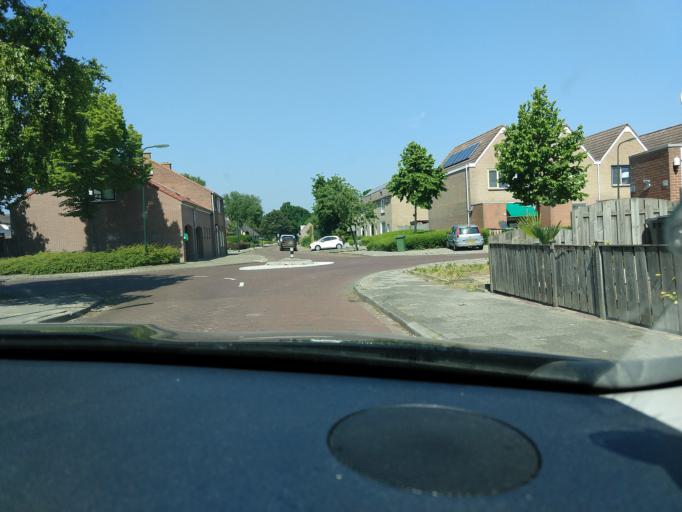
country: NL
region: Zeeland
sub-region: Gemeente Reimerswaal
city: Yerseke
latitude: 51.5485
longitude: 4.0716
